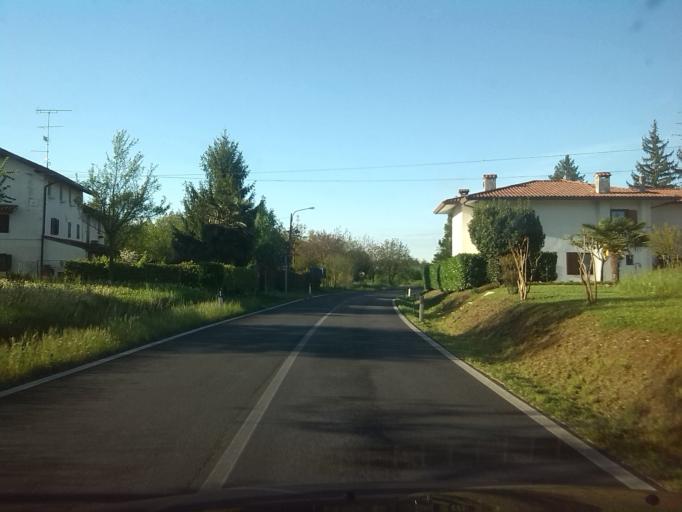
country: IT
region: Friuli Venezia Giulia
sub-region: Provincia di Udine
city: Corno di Rosazzo
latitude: 46.0241
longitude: 13.4410
